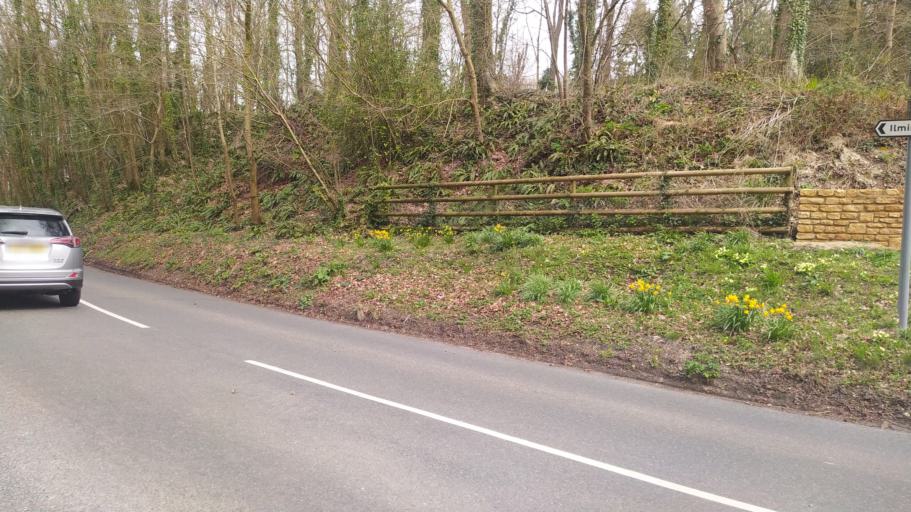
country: GB
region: England
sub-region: Somerset
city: Crewkerne
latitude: 50.8873
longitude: -2.8483
